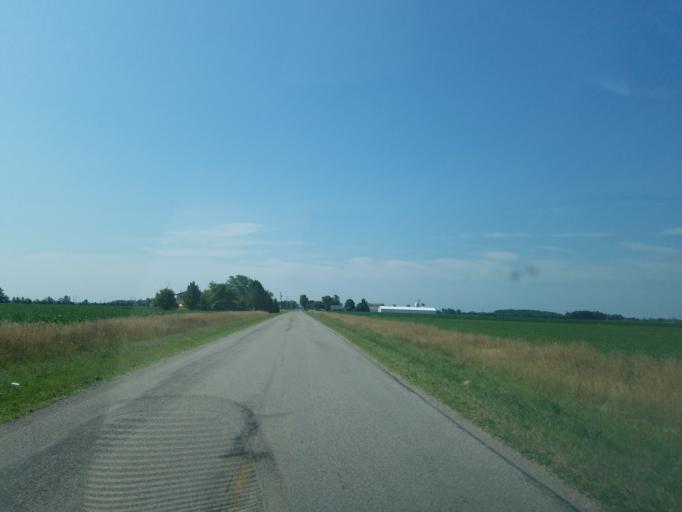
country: US
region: Ohio
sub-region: Van Wert County
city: Van Wert
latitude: 40.9219
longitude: -84.6296
